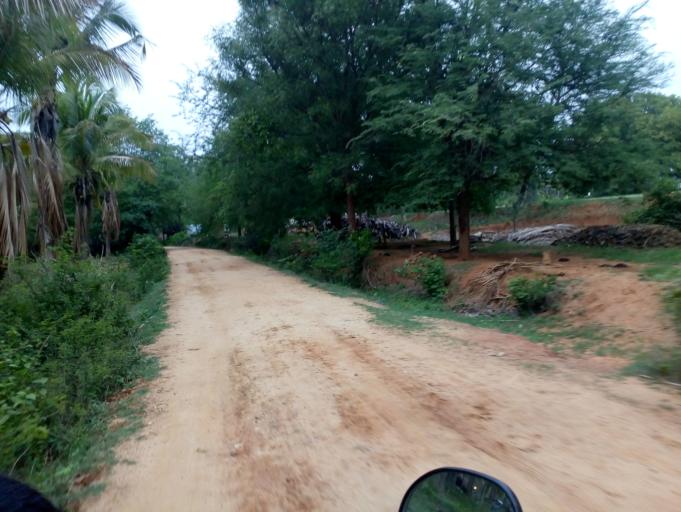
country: IN
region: Karnataka
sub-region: Tumkur
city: Turuvekere
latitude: 13.1935
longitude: 76.7219
